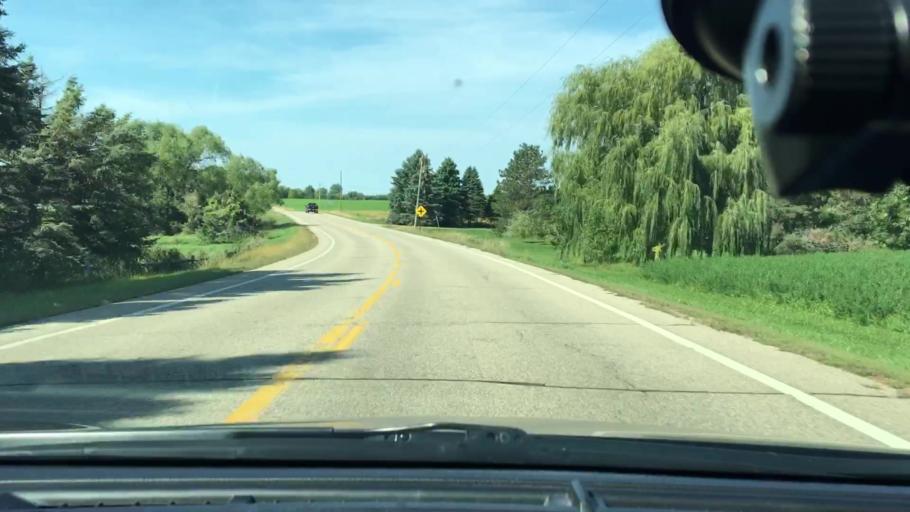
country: US
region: Minnesota
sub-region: Hennepin County
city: Corcoran
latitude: 45.1204
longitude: -93.6022
